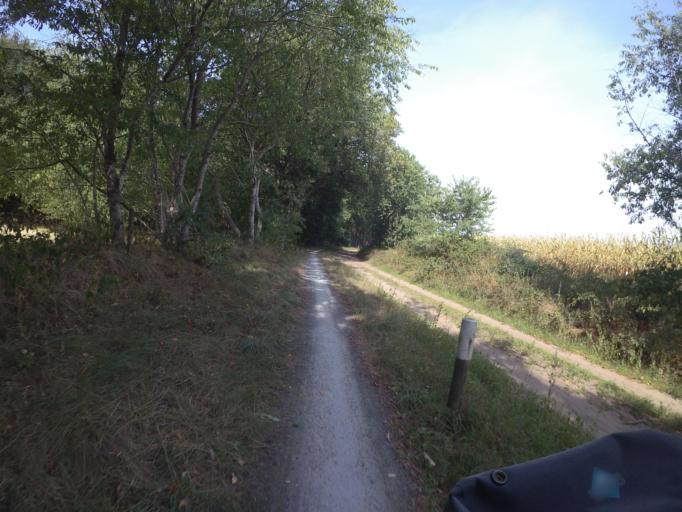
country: NL
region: Drenthe
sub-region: Gemeente Westerveld
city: Havelte
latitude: 52.7824
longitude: 6.2137
